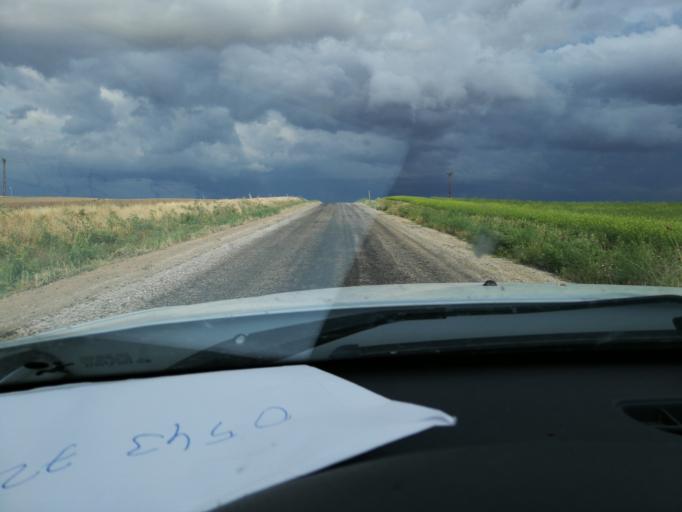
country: TR
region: Kirsehir
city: Kirsehir
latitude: 39.0410
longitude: 34.1740
